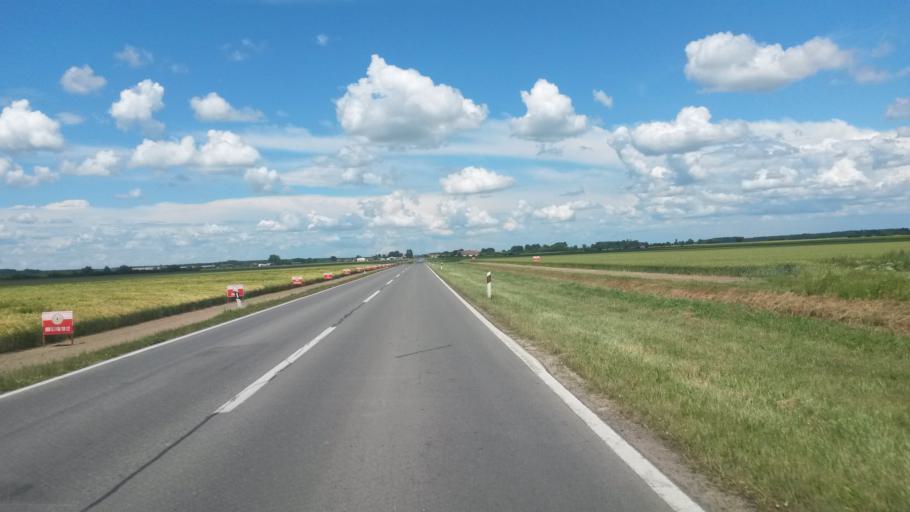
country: HR
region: Osjecko-Baranjska
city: Viskovci
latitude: 45.3863
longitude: 18.4493
